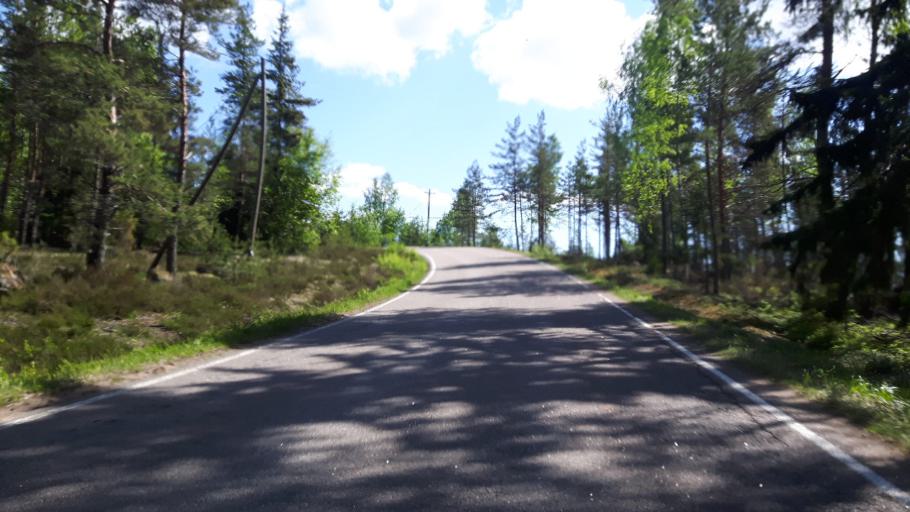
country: FI
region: Kymenlaakso
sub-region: Kotka-Hamina
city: Hamina
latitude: 60.5135
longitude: 27.4153
